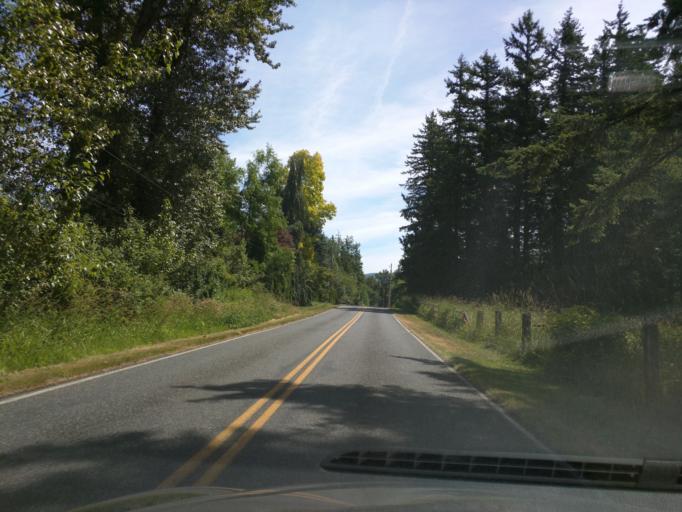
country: US
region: Washington
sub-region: Whatcom County
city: Geneva
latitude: 48.8040
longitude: -122.4257
